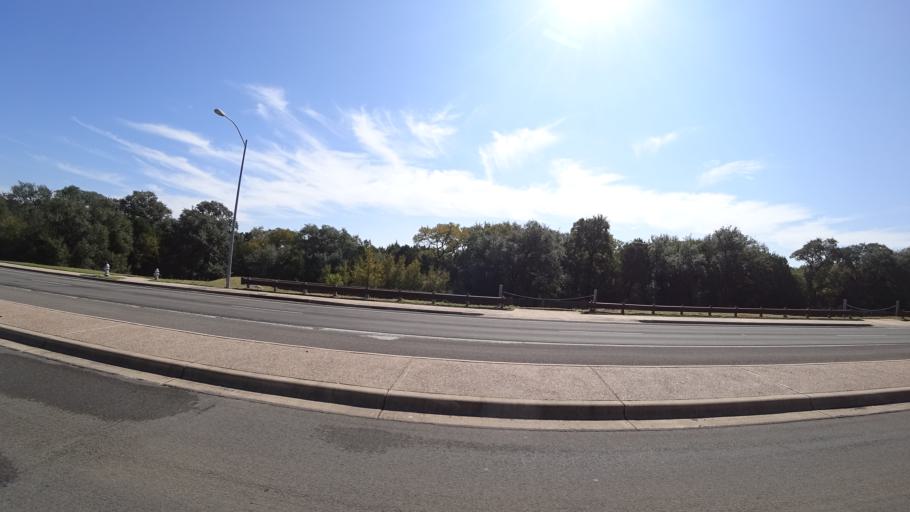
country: US
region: Texas
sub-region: Travis County
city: Shady Hollow
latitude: 30.2081
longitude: -97.8665
